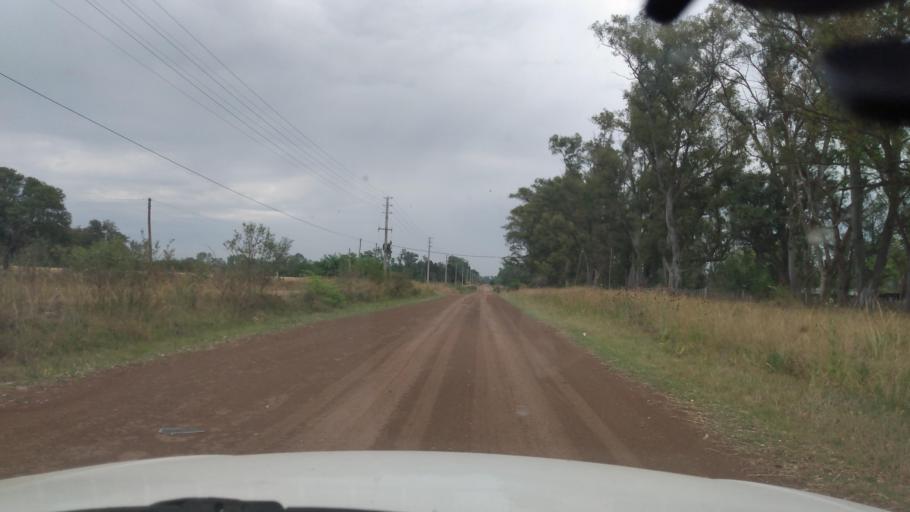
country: AR
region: Buenos Aires
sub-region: Partido de Lujan
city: Lujan
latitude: -34.5534
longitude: -59.1740
